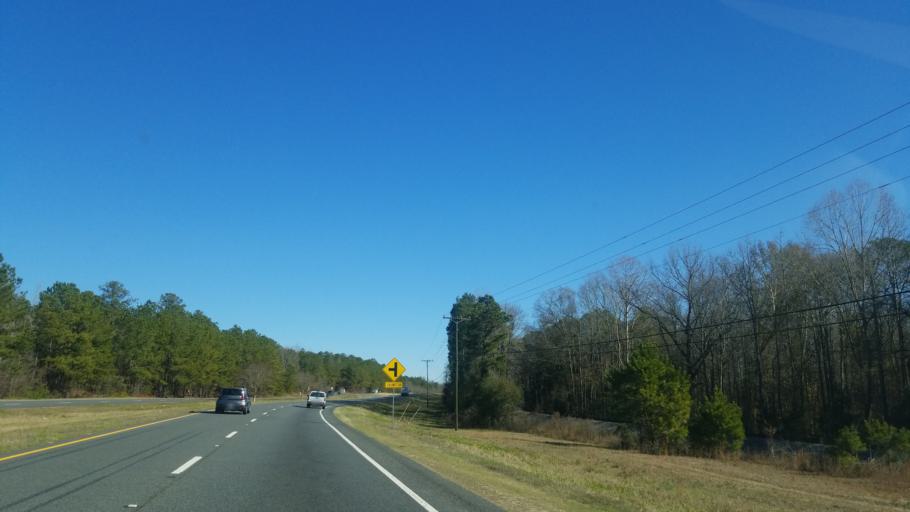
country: US
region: Georgia
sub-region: Muscogee County
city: Columbus
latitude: 32.5461
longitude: -84.8111
